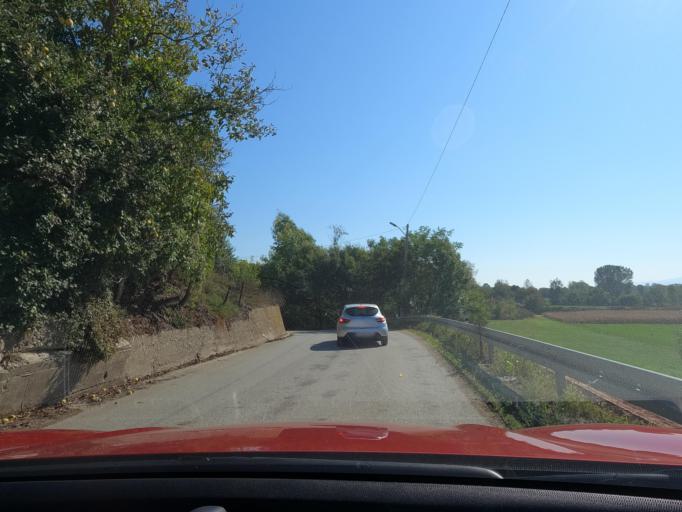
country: RS
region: Central Serbia
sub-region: Raski Okrug
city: Kraljevo
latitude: 43.7675
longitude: 20.6659
